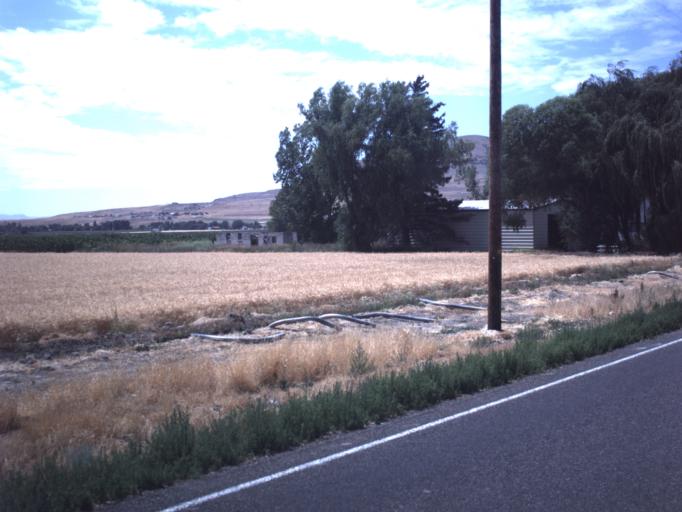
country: US
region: Utah
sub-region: Box Elder County
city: Tremonton
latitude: 41.6947
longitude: -112.2794
